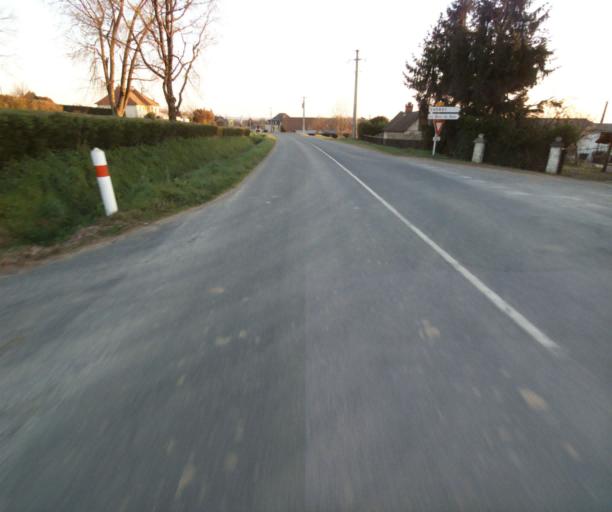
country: FR
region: Limousin
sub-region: Departement de la Correze
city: Sainte-Fereole
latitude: 45.2766
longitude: 1.5629
